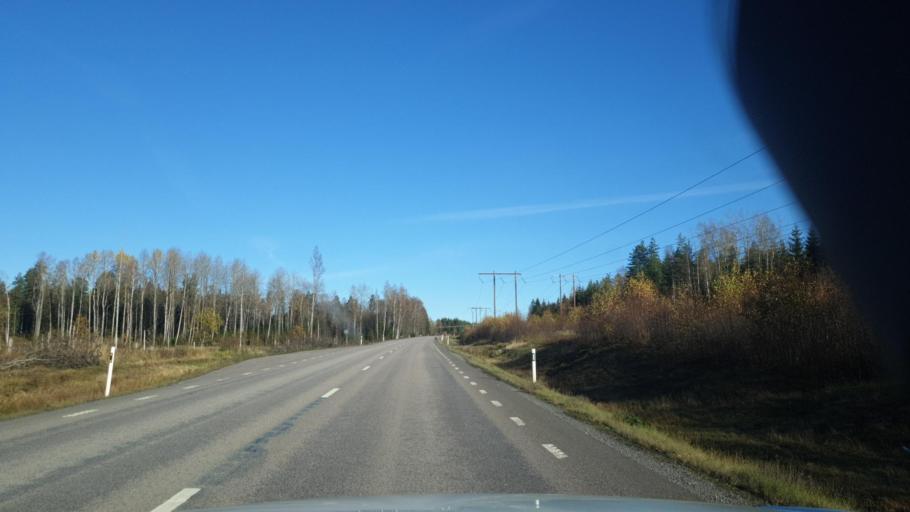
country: SE
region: Vaermland
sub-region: Karlstads Kommun
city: Valberg
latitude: 59.4104
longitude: 13.1832
